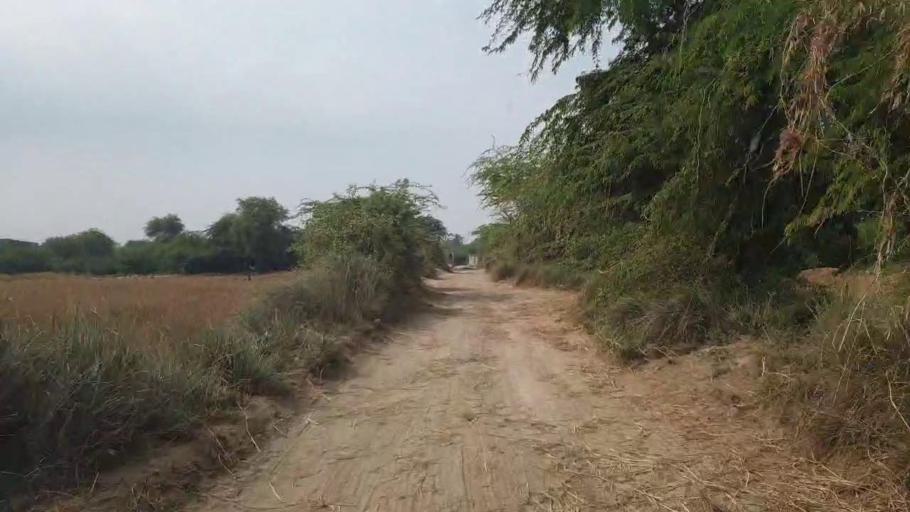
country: PK
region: Sindh
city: Talhar
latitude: 24.8839
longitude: 68.7974
